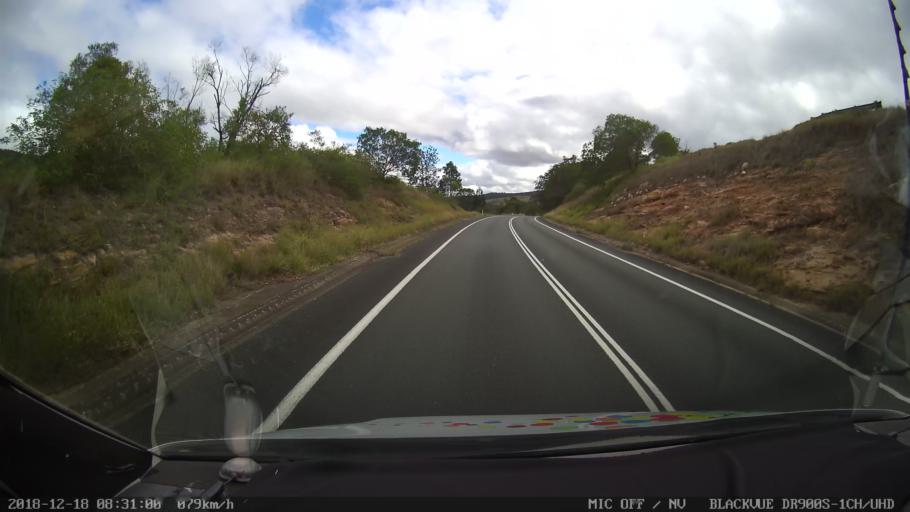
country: AU
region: New South Wales
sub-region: Kyogle
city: Kyogle
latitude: -28.3173
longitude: 152.7743
